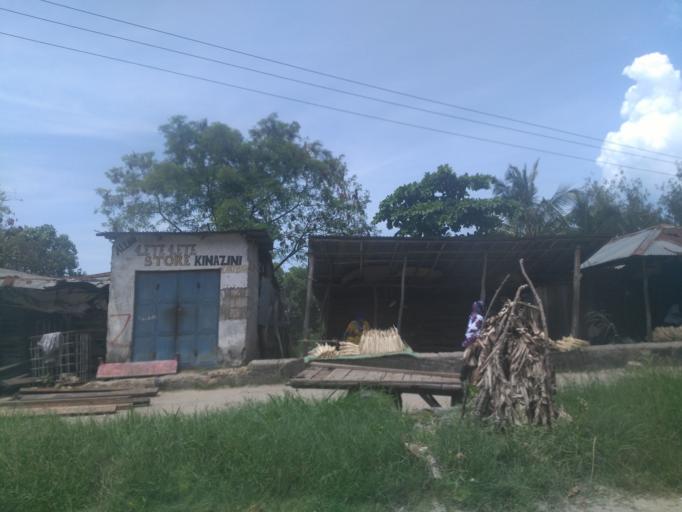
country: TZ
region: Zanzibar Urban/West
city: Zanzibar
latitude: -6.1569
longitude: 39.2046
